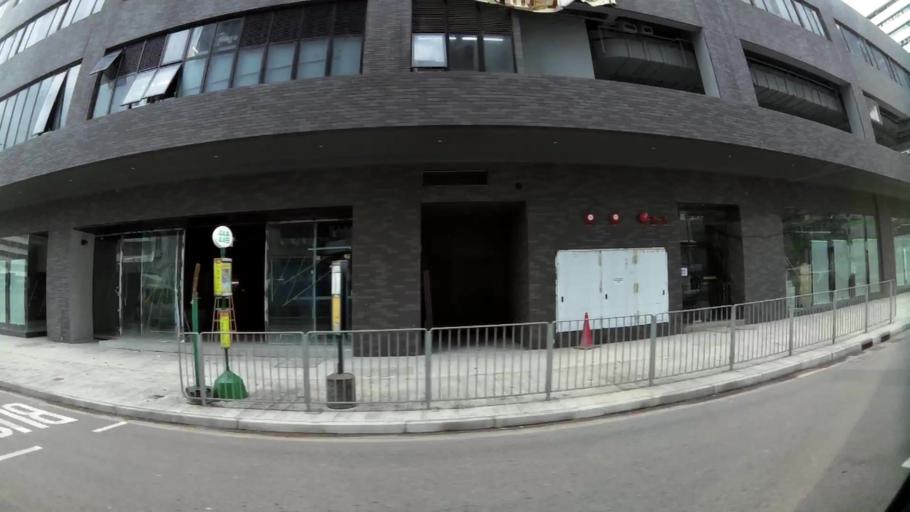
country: HK
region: Tuen Mun
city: Tuen Mun
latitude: 22.3957
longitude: 113.9717
